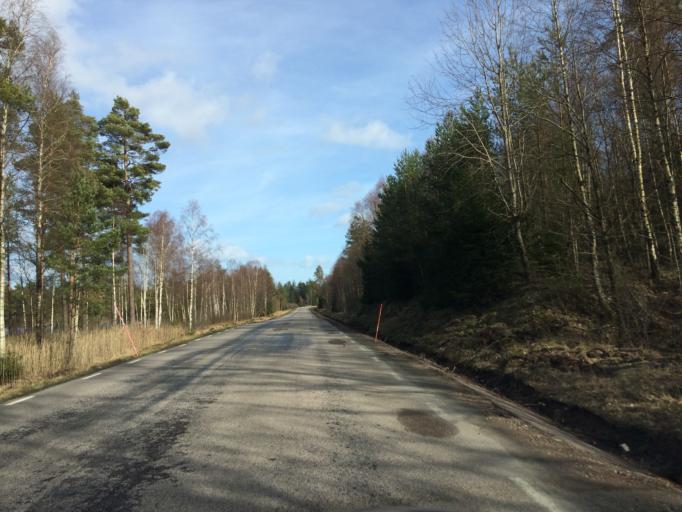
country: SE
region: Halland
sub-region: Hylte Kommun
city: Hyltebruk
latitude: 56.9040
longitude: 13.3887
